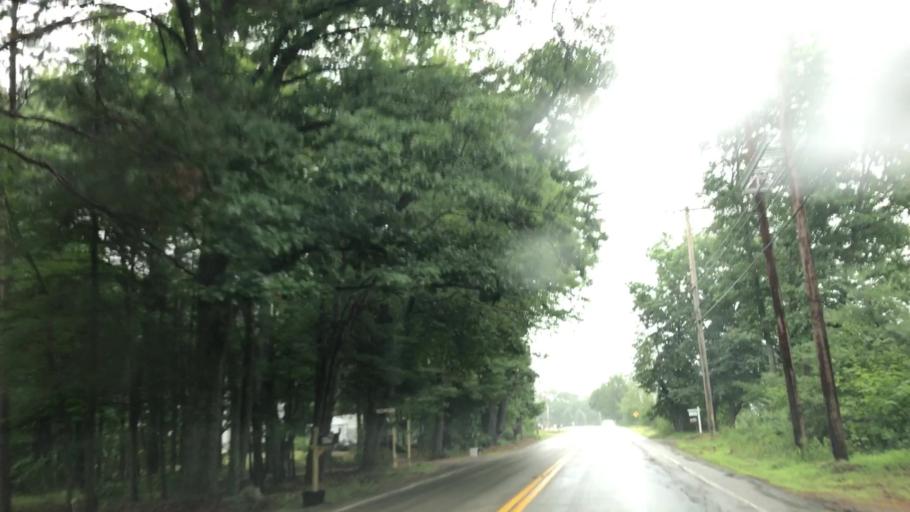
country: US
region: Maine
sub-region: York County
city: South Berwick
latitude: 43.2853
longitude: -70.7938
